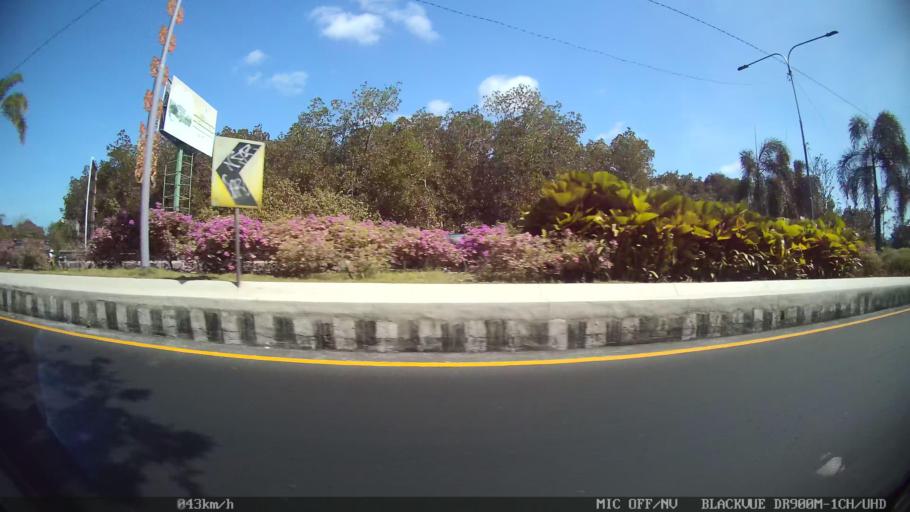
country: ID
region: Bali
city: Jabajero
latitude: -8.7218
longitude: 115.1903
